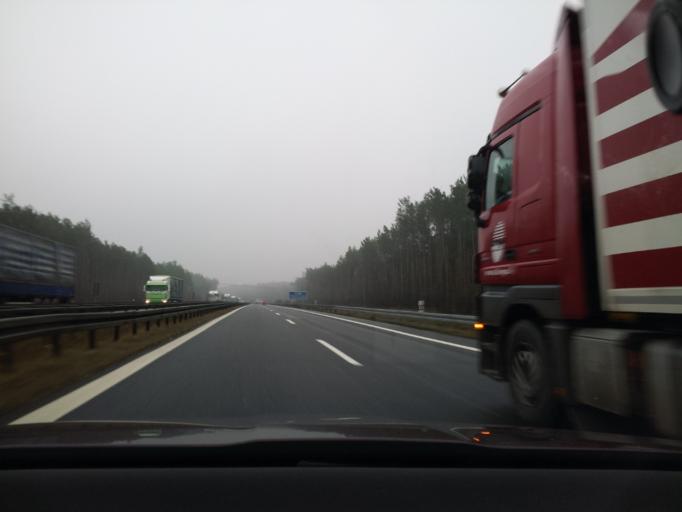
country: DE
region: Brandenburg
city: Spreenhagen
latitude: 52.3146
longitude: 13.9125
